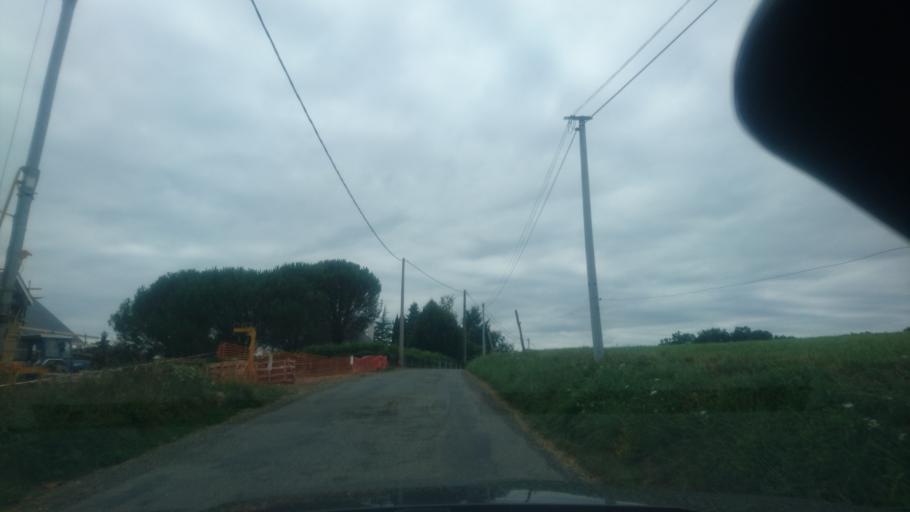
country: FR
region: Midi-Pyrenees
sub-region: Departement des Hautes-Pyrenees
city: Horgues
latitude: 43.1230
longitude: 0.0616
